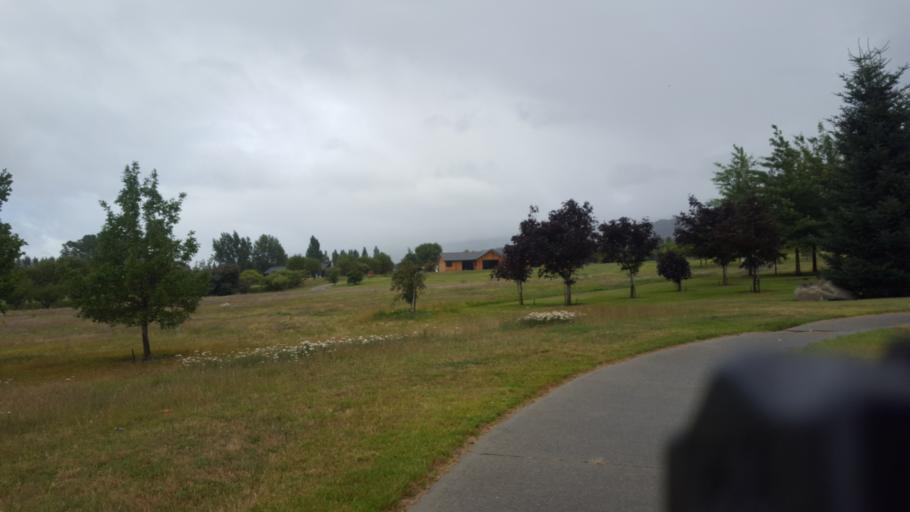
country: NZ
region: Otago
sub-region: Queenstown-Lakes District
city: Wanaka
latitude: -45.1972
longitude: 169.3183
